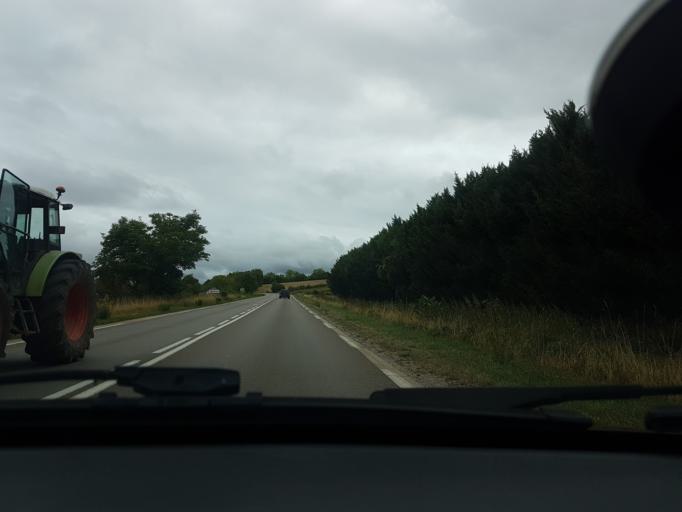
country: FR
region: Bourgogne
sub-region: Departement de l'Yonne
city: Champs-sur-Yonne
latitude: 47.7000
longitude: 3.6307
